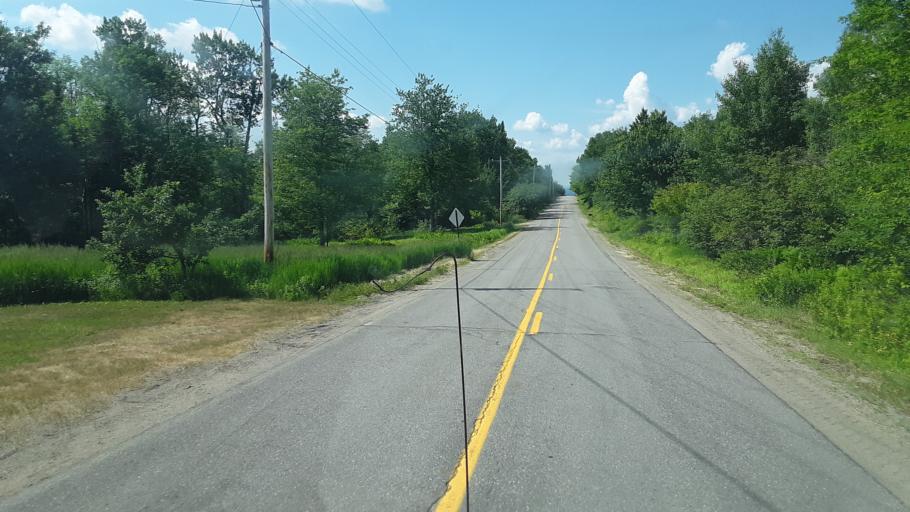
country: US
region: Maine
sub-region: Washington County
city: Calais
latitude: 45.0878
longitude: -67.5033
